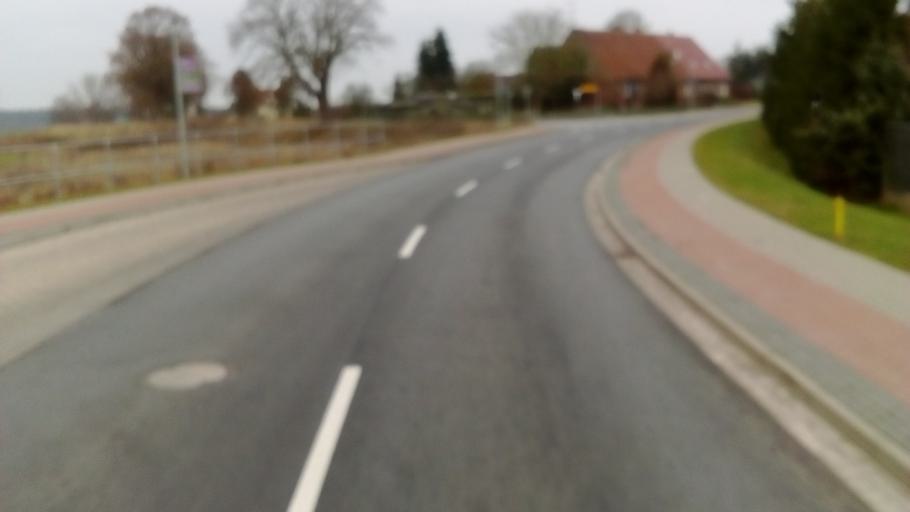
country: DE
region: Mecklenburg-Vorpommern
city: Loitz
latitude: 53.4224
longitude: 13.4279
